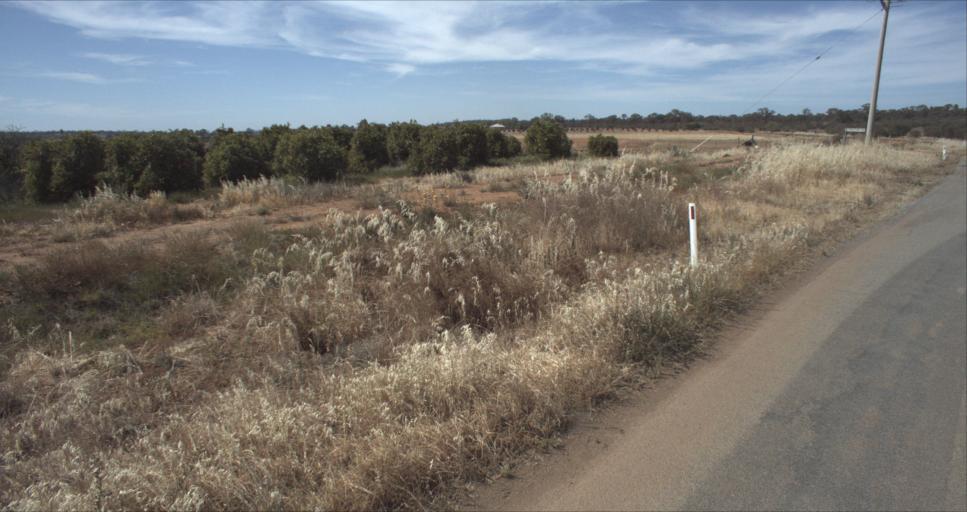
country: AU
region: New South Wales
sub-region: Leeton
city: Leeton
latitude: -34.5774
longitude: 146.4555
